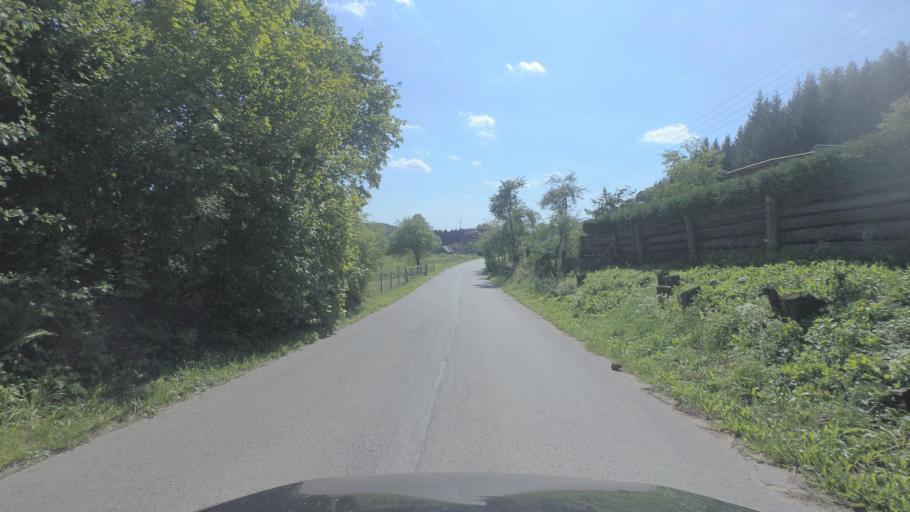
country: LT
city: Nemencine
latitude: 54.8481
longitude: 25.3736
